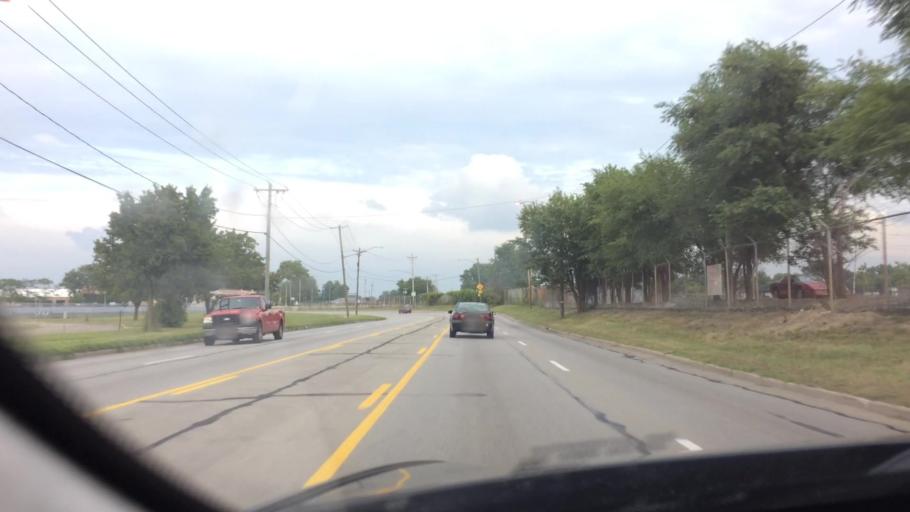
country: US
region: Ohio
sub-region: Wood County
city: Rossford
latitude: 41.6380
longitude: -83.5964
